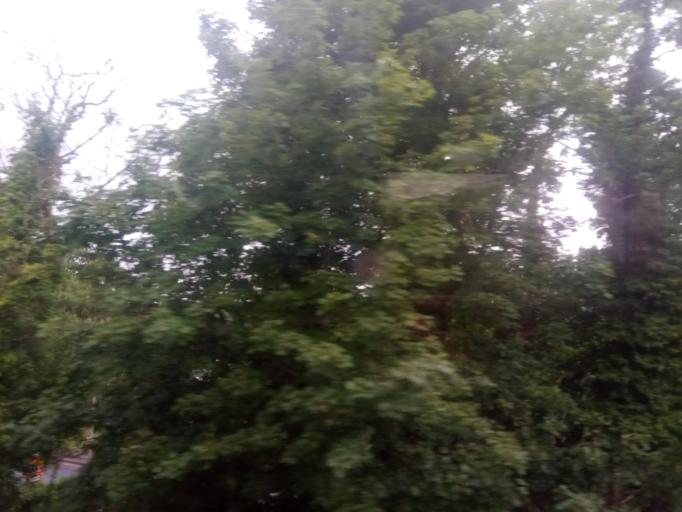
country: GB
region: England
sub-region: North Yorkshire
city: Settle
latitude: 54.0682
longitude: -2.2800
